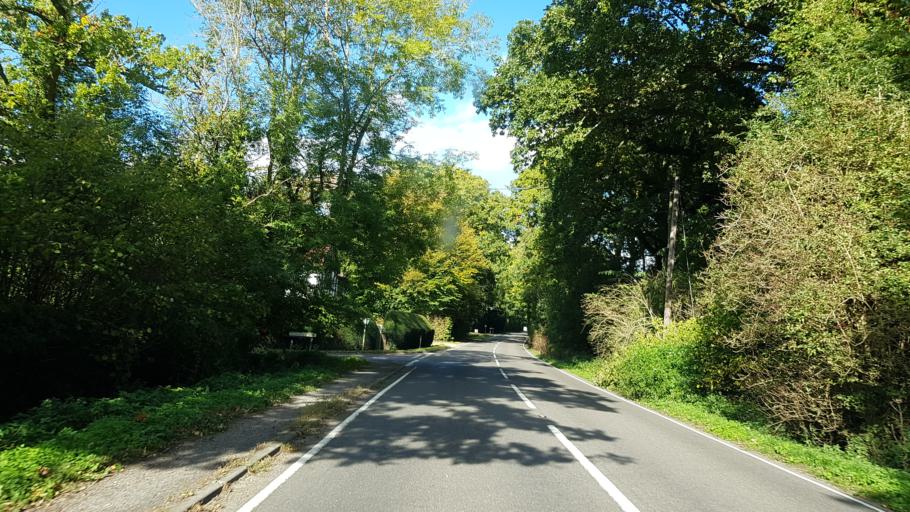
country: GB
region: England
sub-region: Surrey
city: Chiddingfold
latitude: 51.0900
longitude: -0.6446
